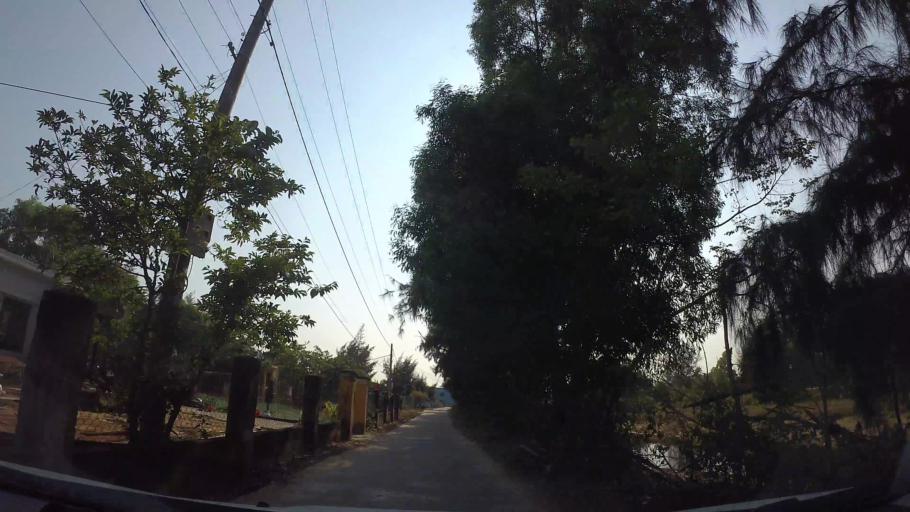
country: VN
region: Da Nang
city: Ngu Hanh Son
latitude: 15.9552
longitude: 108.2610
